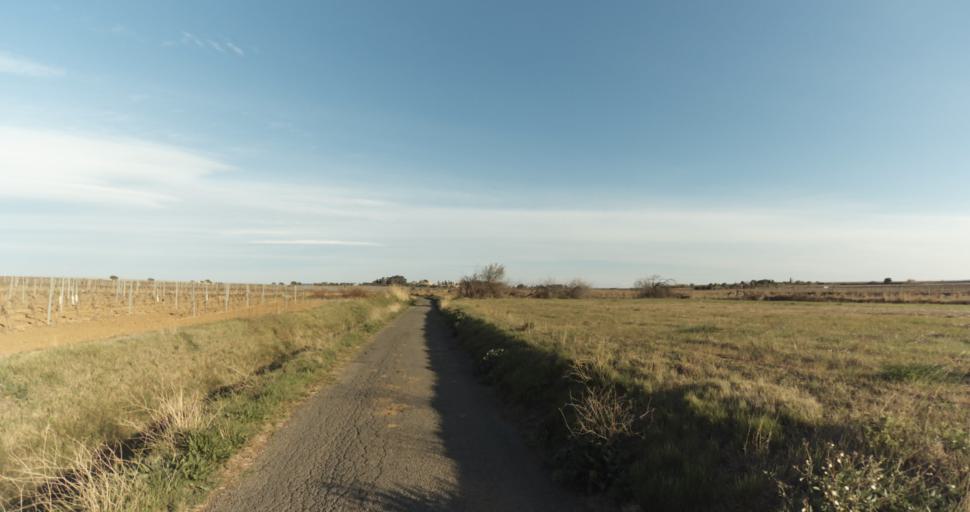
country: FR
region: Languedoc-Roussillon
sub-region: Departement de l'Herault
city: Marseillan
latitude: 43.3740
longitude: 3.5255
